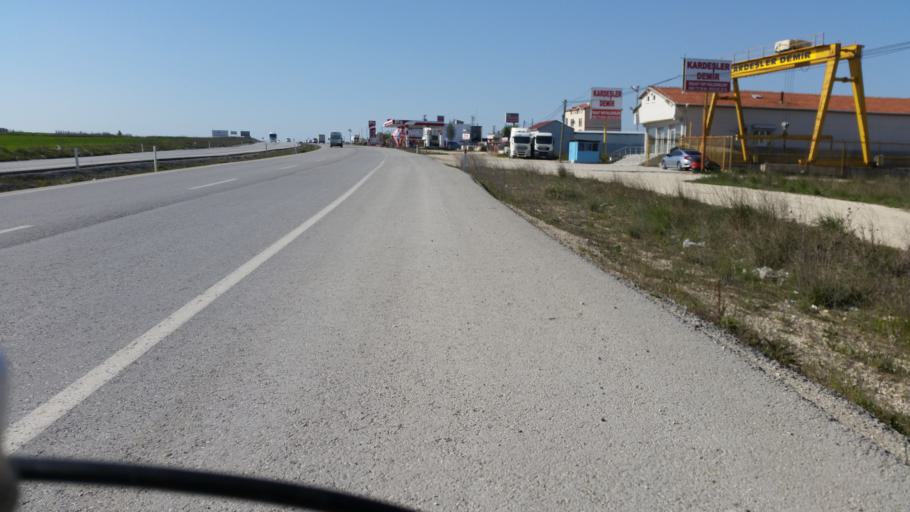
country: TR
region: Tekirdag
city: Cerkezkoey
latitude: 41.3397
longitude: 27.9662
